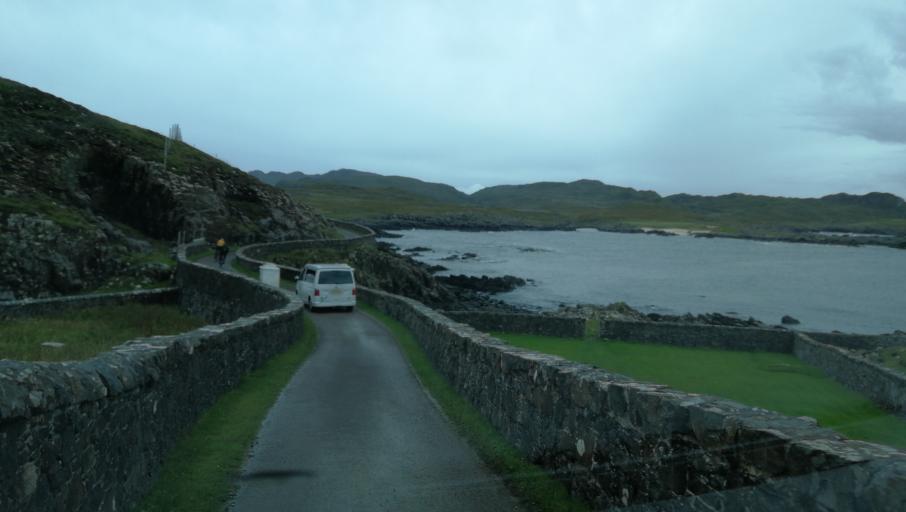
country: GB
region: Scotland
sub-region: Argyll and Bute
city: Isle Of Mull
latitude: 56.7201
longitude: -6.2234
